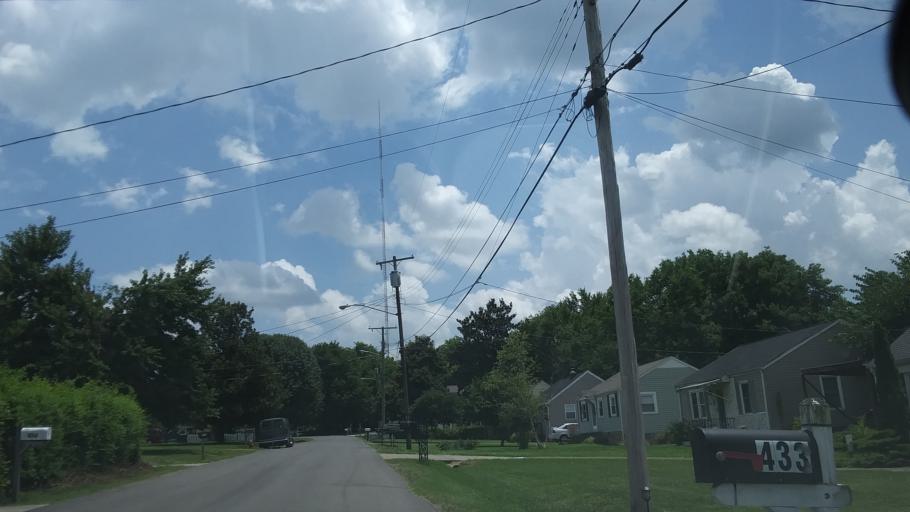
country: US
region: Tennessee
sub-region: Davidson County
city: Belle Meade
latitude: 36.1489
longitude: -86.8715
